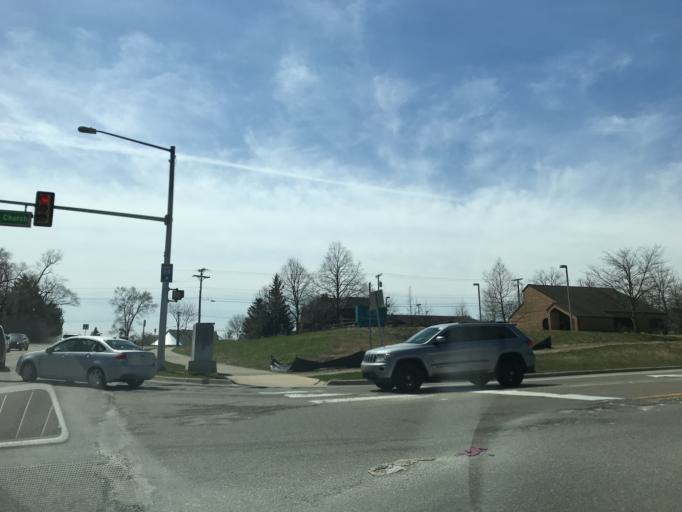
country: US
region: Michigan
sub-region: Washtenaw County
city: Ann Arbor
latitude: 42.2571
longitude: -83.7502
